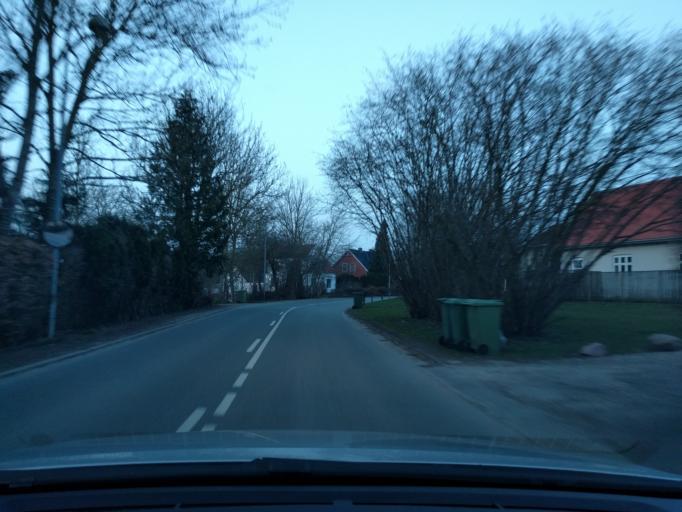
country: DK
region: South Denmark
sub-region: Odense Kommune
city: Bellinge
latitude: 55.3494
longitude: 10.2716
